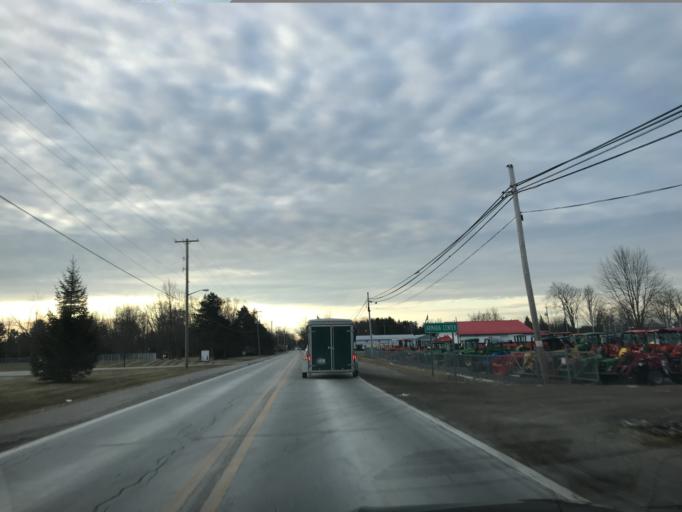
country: US
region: Michigan
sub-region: Macomb County
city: Armada
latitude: 42.8532
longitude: -82.8850
